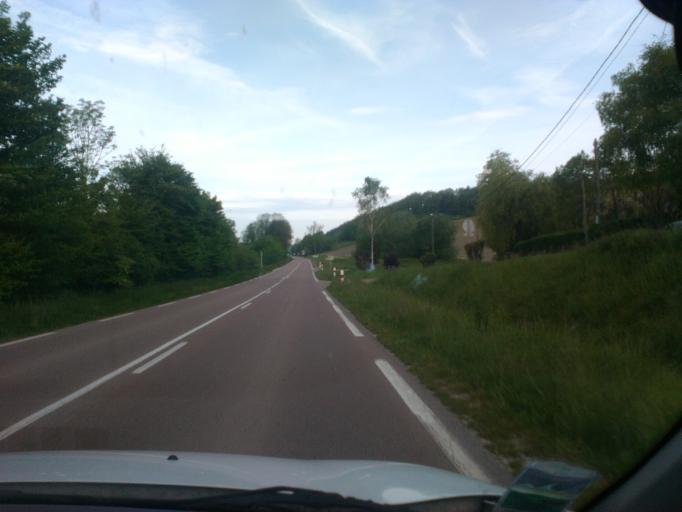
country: FR
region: Champagne-Ardenne
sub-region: Departement de l'Aube
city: Bar-sur-Aube
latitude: 48.2704
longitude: 4.6395
